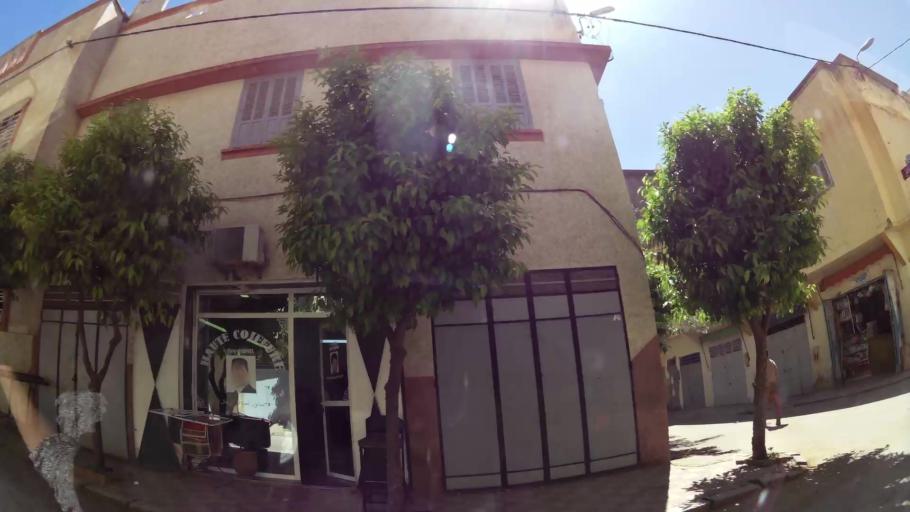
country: MA
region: Meknes-Tafilalet
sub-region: Meknes
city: Meknes
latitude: 33.8729
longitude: -5.5635
